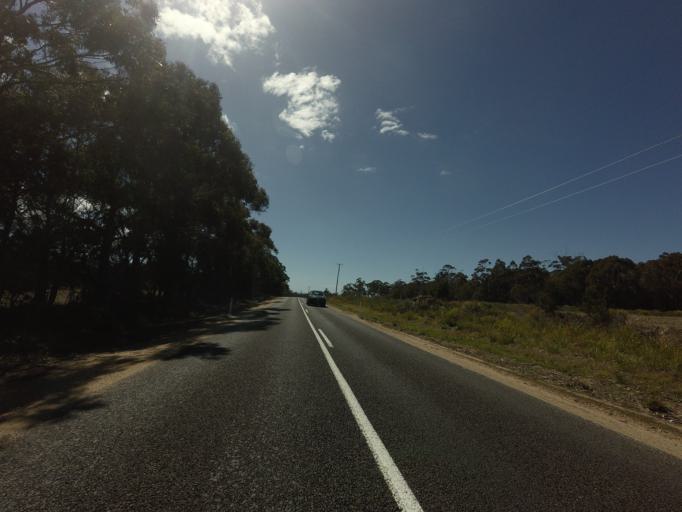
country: AU
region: Tasmania
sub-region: Break O'Day
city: St Helens
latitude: -41.6951
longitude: 148.2792
